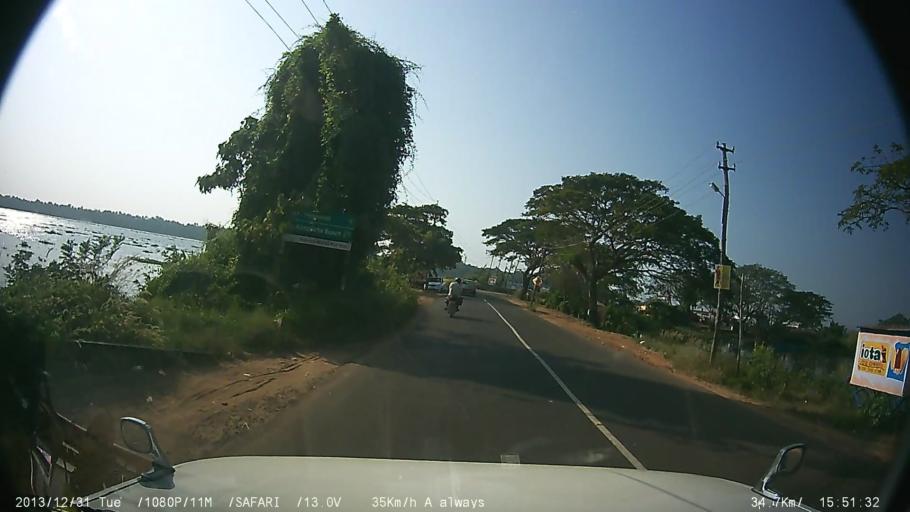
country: IN
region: Kerala
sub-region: Alappuzha
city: Shertallai
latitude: 9.6739
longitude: 76.3987
